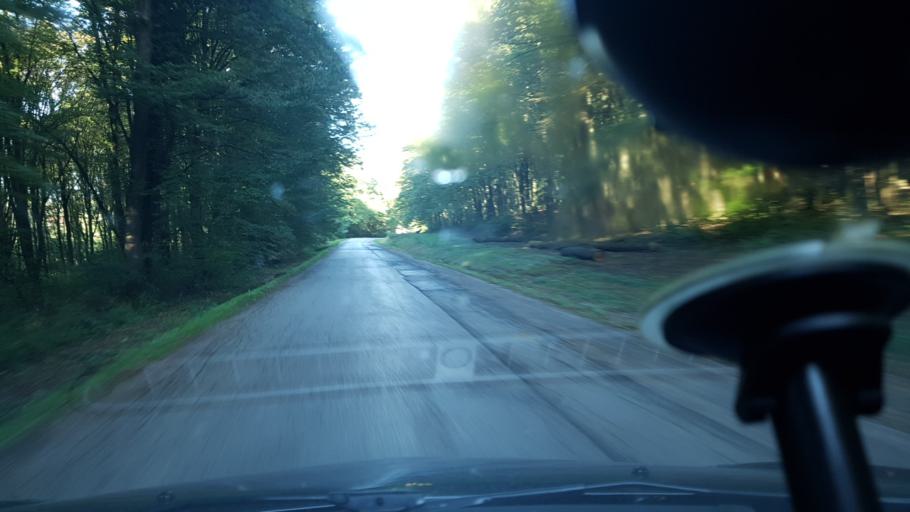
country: HR
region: Bjelovarsko-Bilogorska
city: Bjelovar
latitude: 45.9305
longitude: 16.8673
